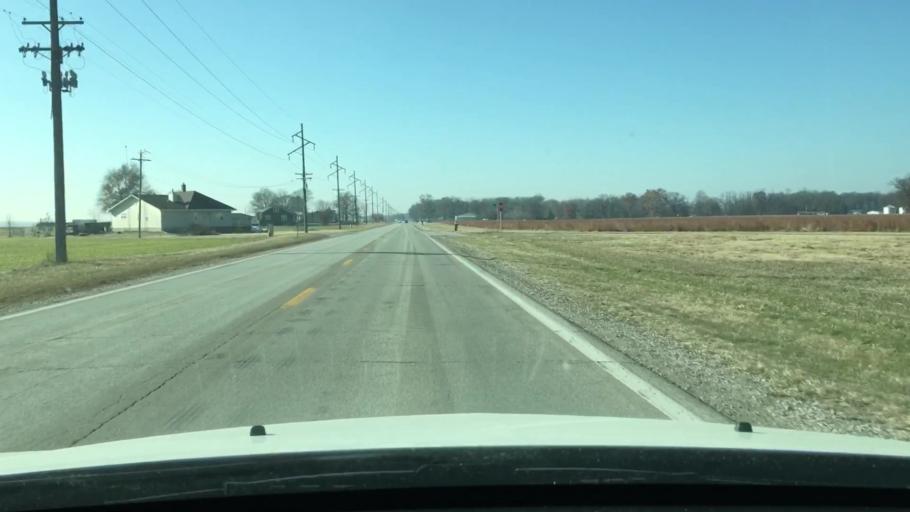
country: US
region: Illinois
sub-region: Cass County
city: Beardstown
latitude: 39.9880
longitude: -90.4414
